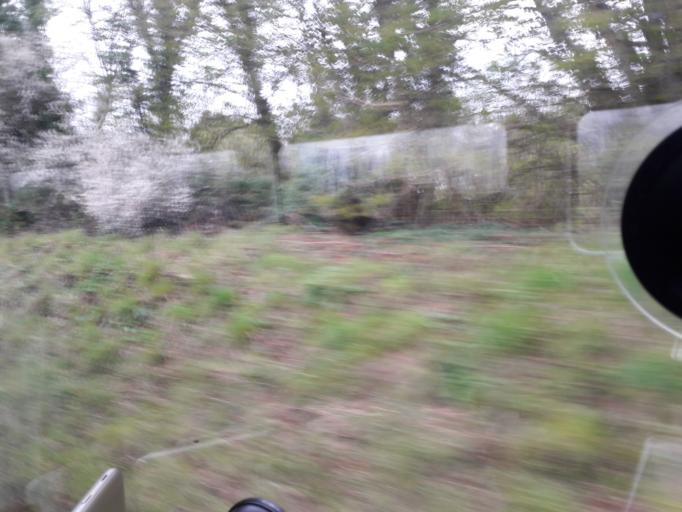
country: IE
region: Leinster
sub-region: An Longfort
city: Longford
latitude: 53.7243
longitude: -7.7697
